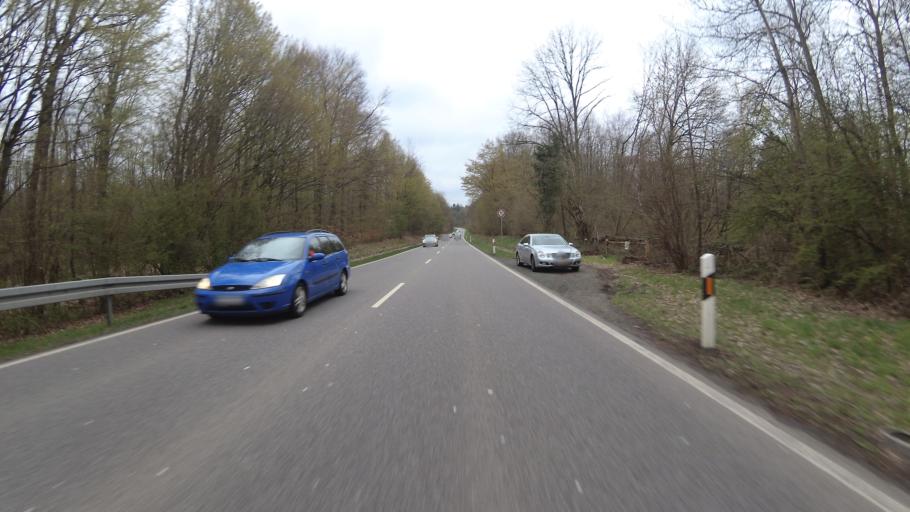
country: DE
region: Saarland
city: Merchweiler
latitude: 49.3474
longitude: 7.0769
